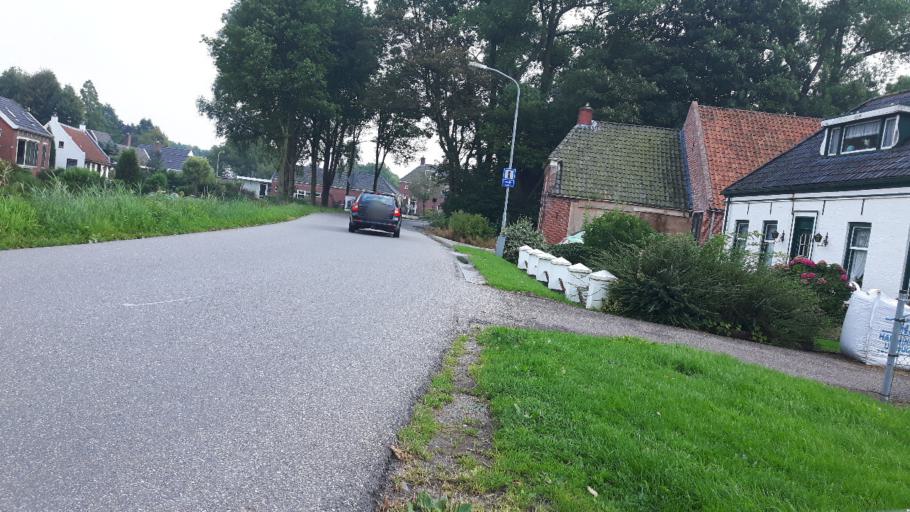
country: NL
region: Groningen
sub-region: Gemeente Bedum
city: Bedum
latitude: 53.3508
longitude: 6.6430
